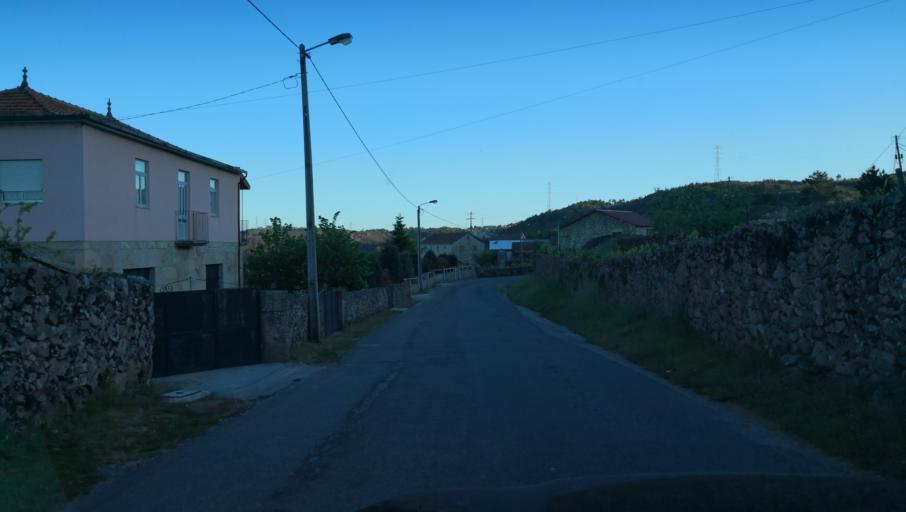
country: PT
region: Vila Real
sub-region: Sabrosa
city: Sabrosa
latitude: 41.3466
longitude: -7.6203
